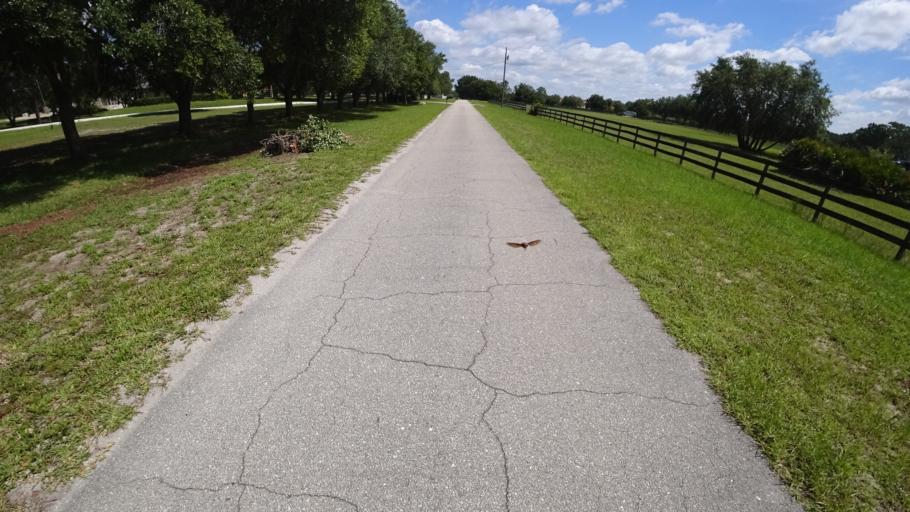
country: US
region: Florida
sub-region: Sarasota County
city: The Meadows
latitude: 27.4152
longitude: -82.3265
